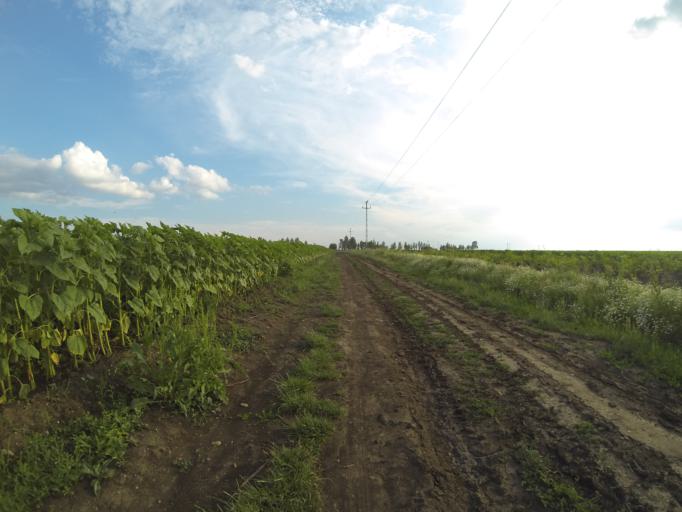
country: RO
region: Dolj
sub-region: Comuna Caloparu
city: Salcuta
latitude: 44.1461
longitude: 23.6974
